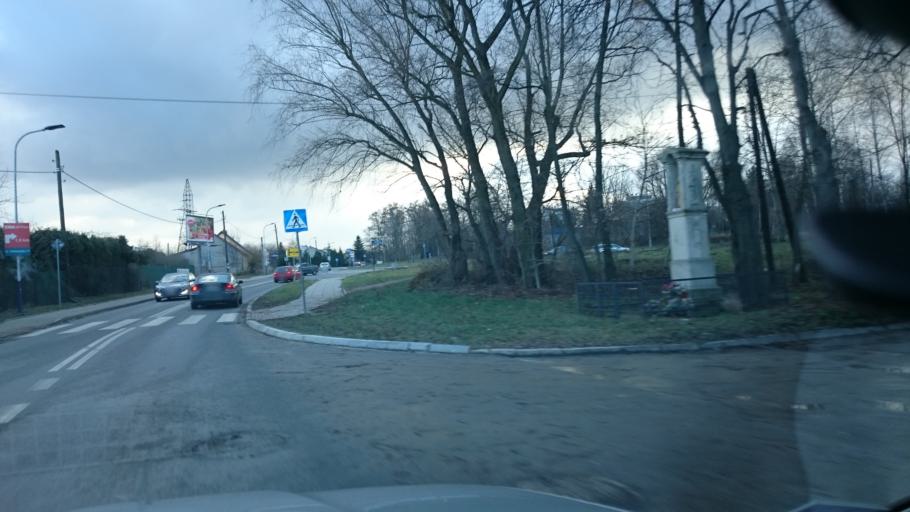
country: PL
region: Lesser Poland Voivodeship
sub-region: Powiat wielicki
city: Czarnochowice
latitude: 50.0154
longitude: 20.0283
